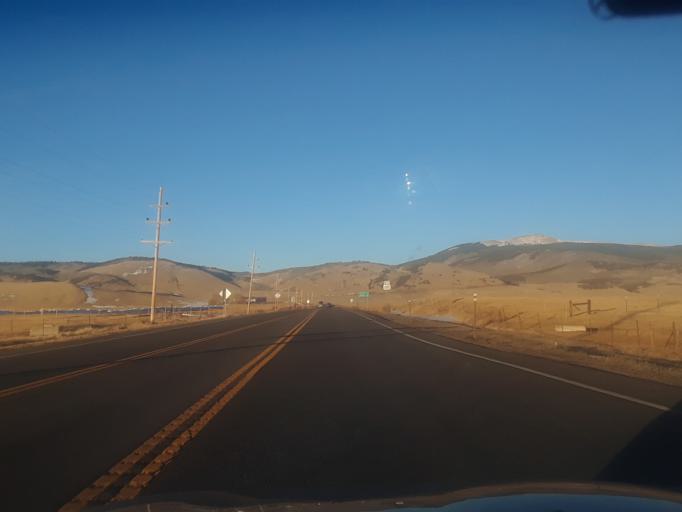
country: US
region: Colorado
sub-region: Park County
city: Fairplay
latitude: 39.3789
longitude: -105.7986
